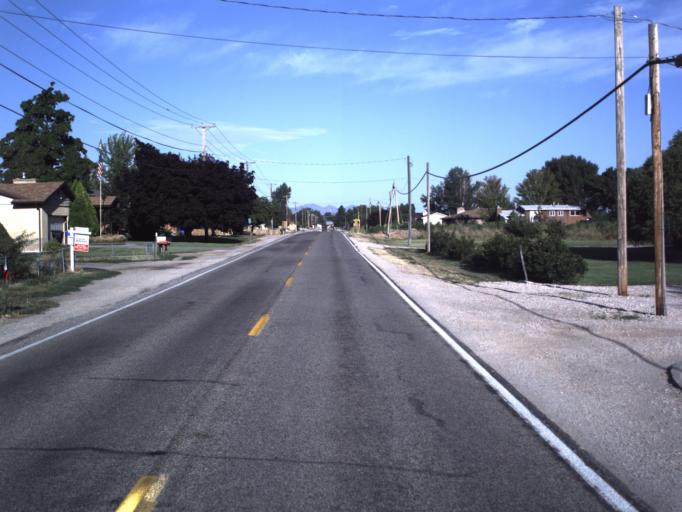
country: US
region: Utah
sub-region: Weber County
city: Plain City
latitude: 41.3052
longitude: -112.0693
